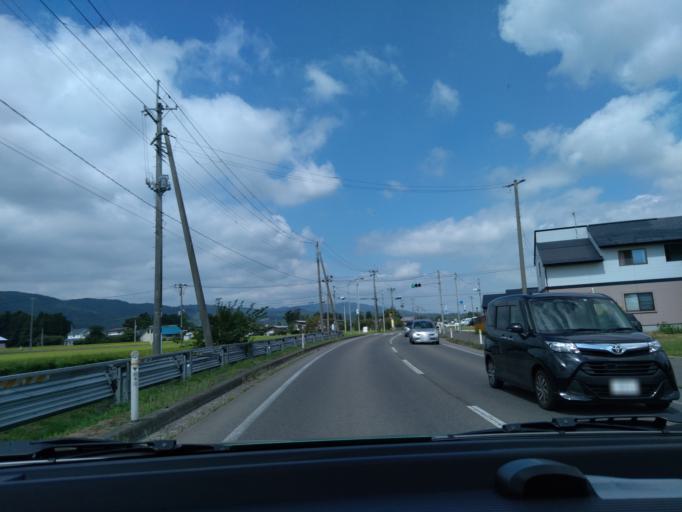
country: JP
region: Iwate
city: Hanamaki
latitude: 39.4465
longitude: 141.0977
